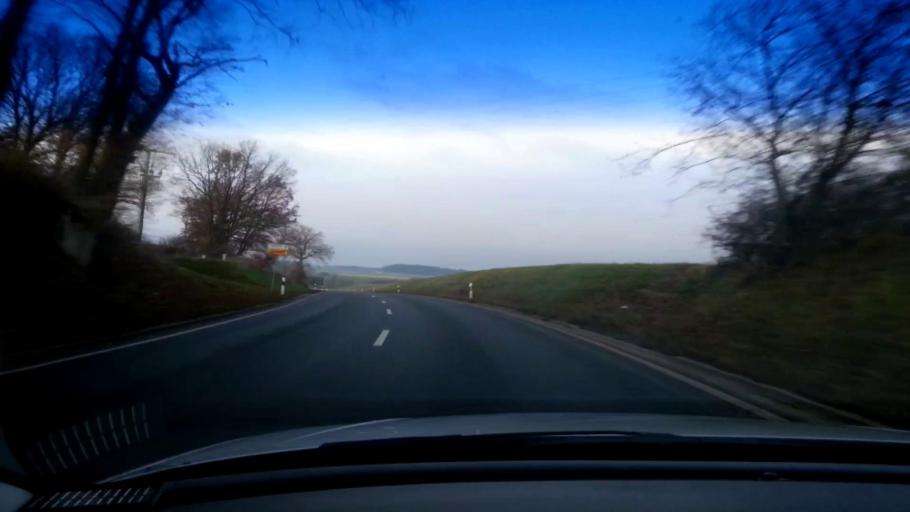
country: DE
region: Bavaria
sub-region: Upper Franconia
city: Pommersfelden
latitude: 49.7796
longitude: 10.8255
